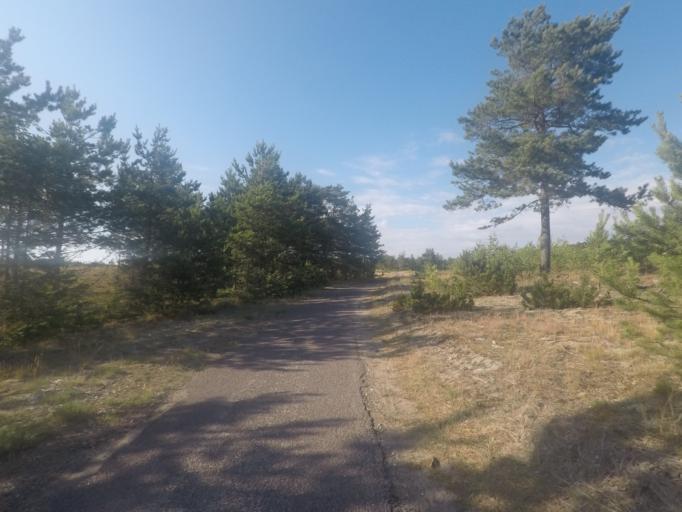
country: LT
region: Klaipedos apskritis
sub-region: Klaipeda
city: Klaipeda
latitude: 55.5946
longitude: 21.1151
